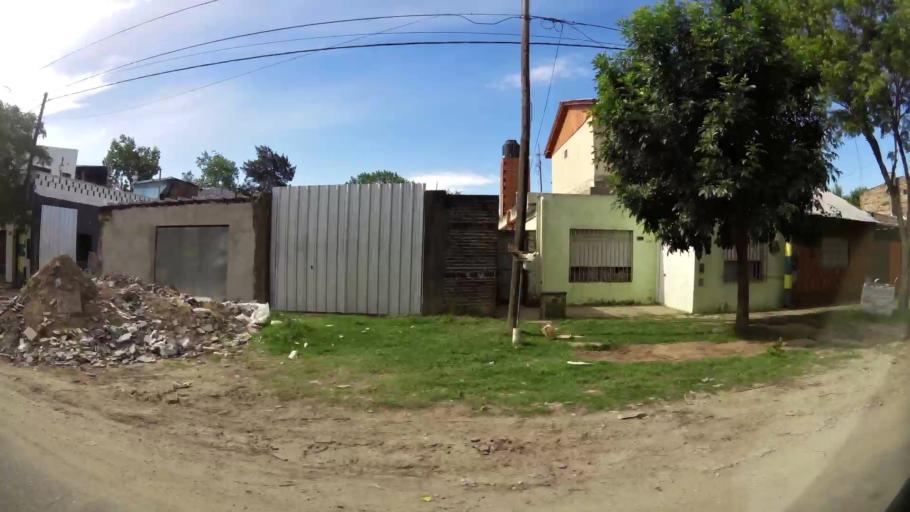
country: AR
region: Santa Fe
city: Granadero Baigorria
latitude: -32.9245
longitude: -60.7184
